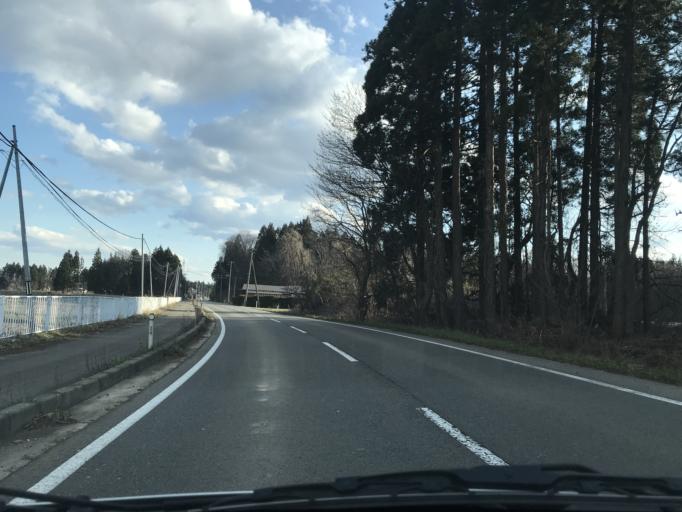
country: JP
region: Iwate
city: Kitakami
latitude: 39.3325
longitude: 141.0392
